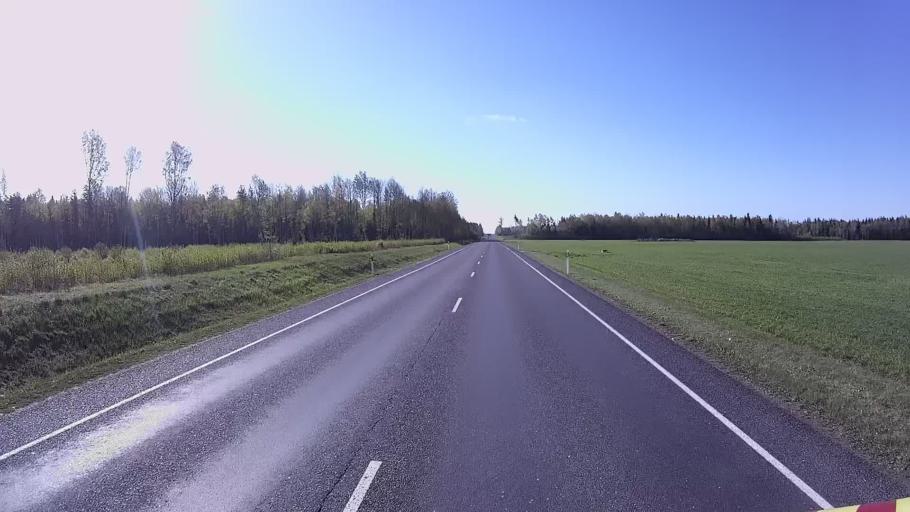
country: EE
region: Viljandimaa
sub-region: Vohma linn
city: Vohma
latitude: 58.7239
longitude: 25.6020
